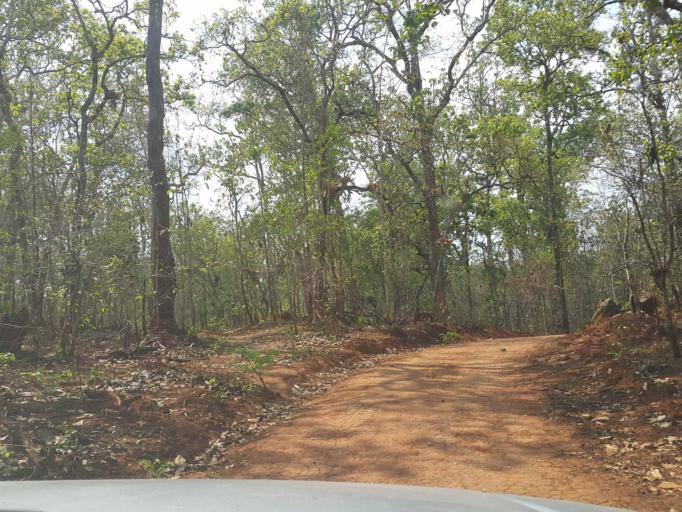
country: TH
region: Chiang Mai
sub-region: Amphoe Chiang Dao
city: Chiang Dao
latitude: 19.3226
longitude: 98.7212
